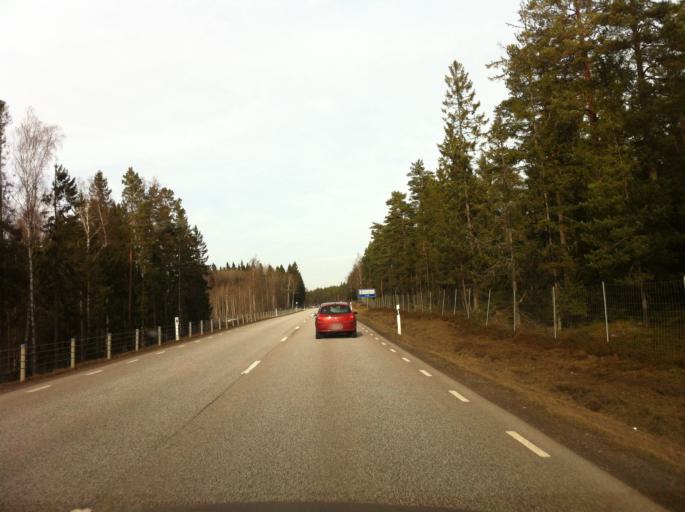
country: SE
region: Vaestra Goetaland
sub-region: Gullspangs Kommun
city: Gullspang
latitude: 58.9172
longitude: 14.0280
